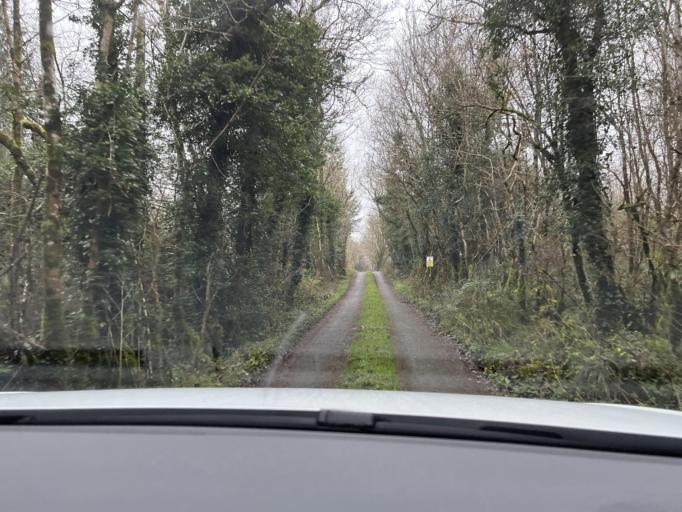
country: IE
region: Connaught
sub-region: County Leitrim
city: Manorhamilton
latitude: 54.2845
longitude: -8.1159
